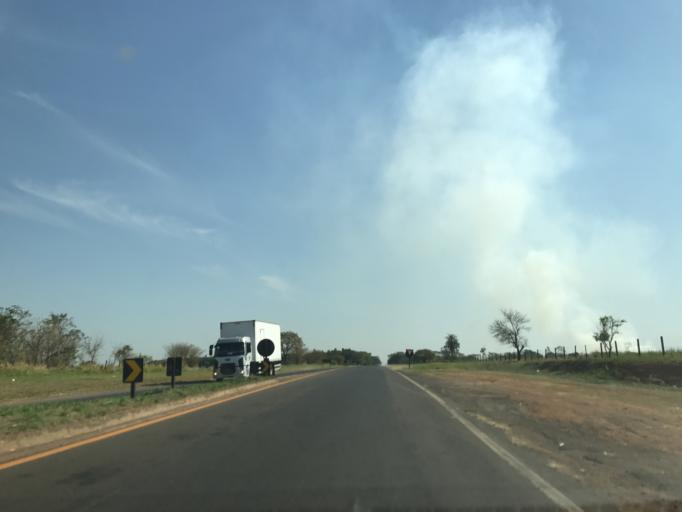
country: BR
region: Sao Paulo
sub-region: Penapolis
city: Penapolis
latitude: -21.3868
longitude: -50.0967
